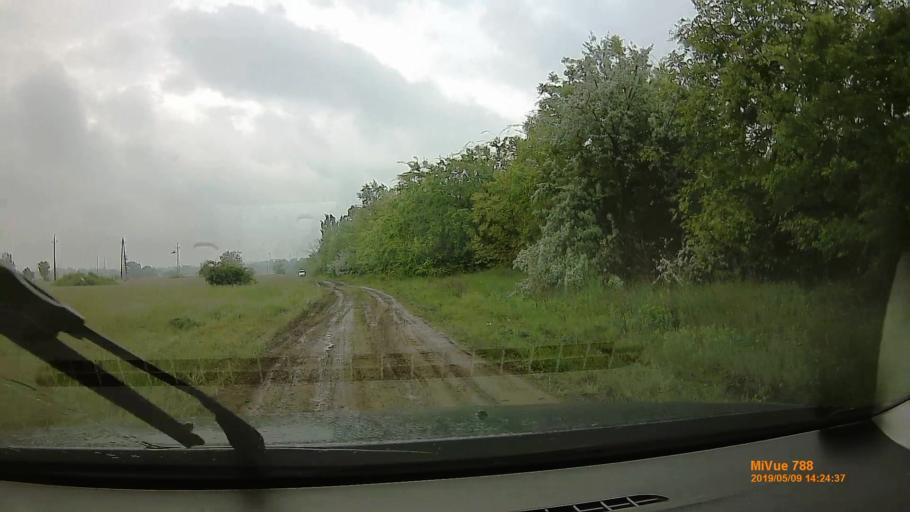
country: HU
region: Budapest
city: Budapest XVI. keruelet
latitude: 47.4994
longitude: 19.2129
